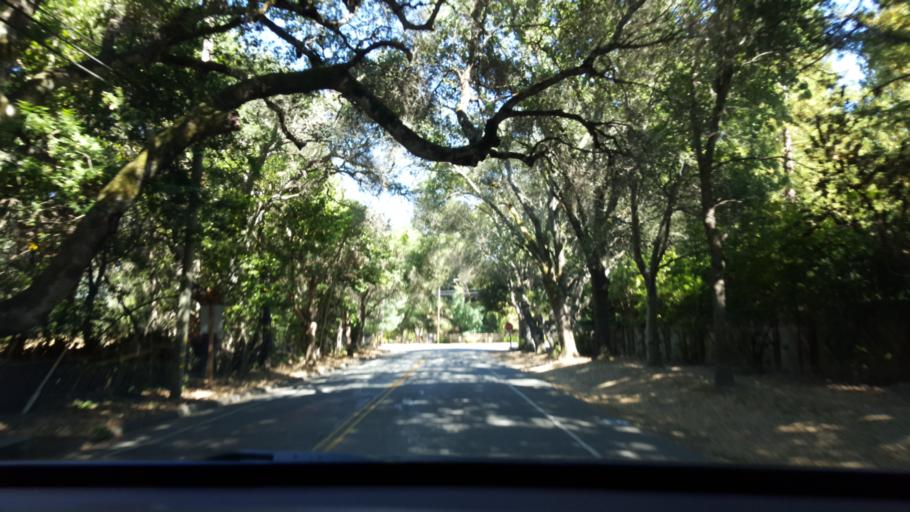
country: US
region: California
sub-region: San Mateo County
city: Woodside
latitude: 37.4265
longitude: -122.2670
